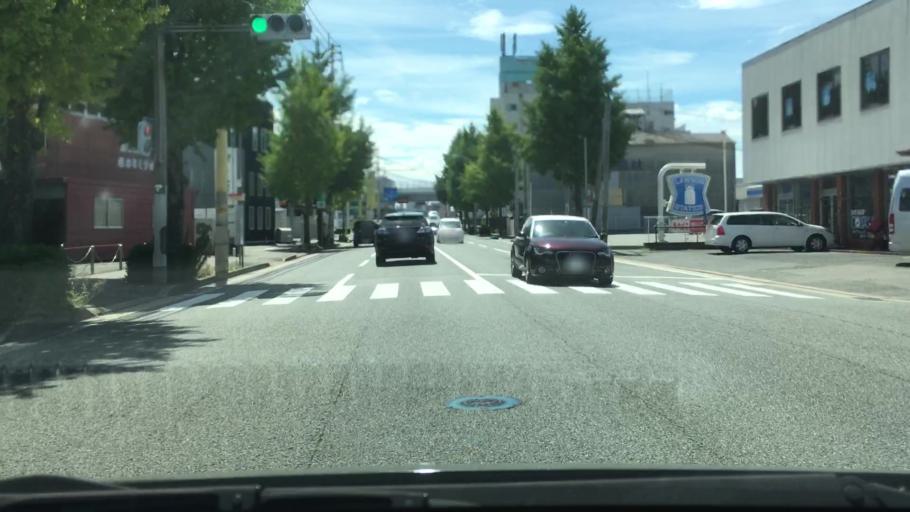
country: JP
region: Fukuoka
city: Onojo
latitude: 33.5573
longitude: 130.4516
